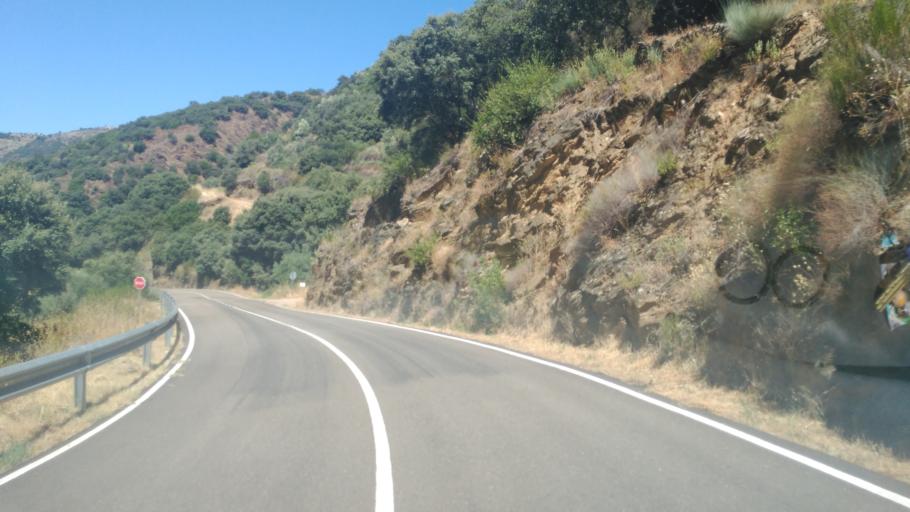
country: ES
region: Castille and Leon
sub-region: Provincia de Salamanca
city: Mieza
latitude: 41.1891
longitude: -6.6797
